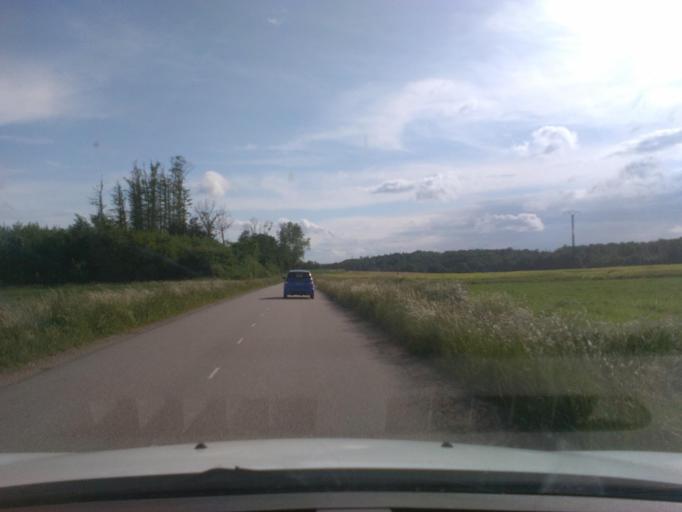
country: FR
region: Lorraine
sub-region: Departement de Meurthe-et-Moselle
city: Baccarat
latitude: 48.5100
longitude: 6.7153
